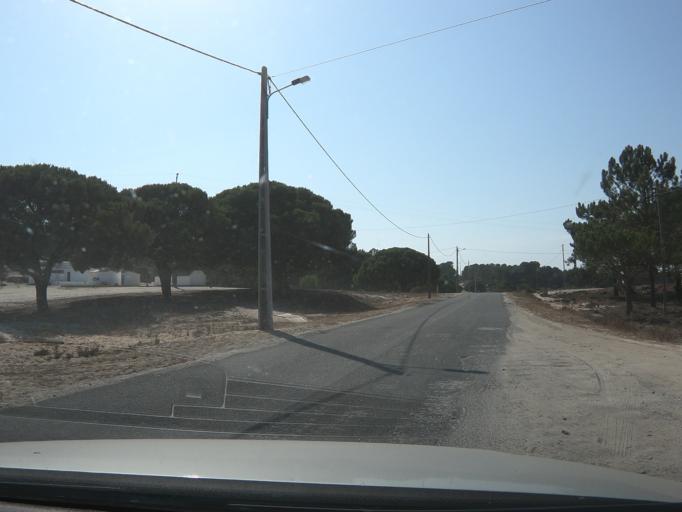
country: PT
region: Setubal
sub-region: Setubal
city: Setubal
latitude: 38.4003
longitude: -8.7635
